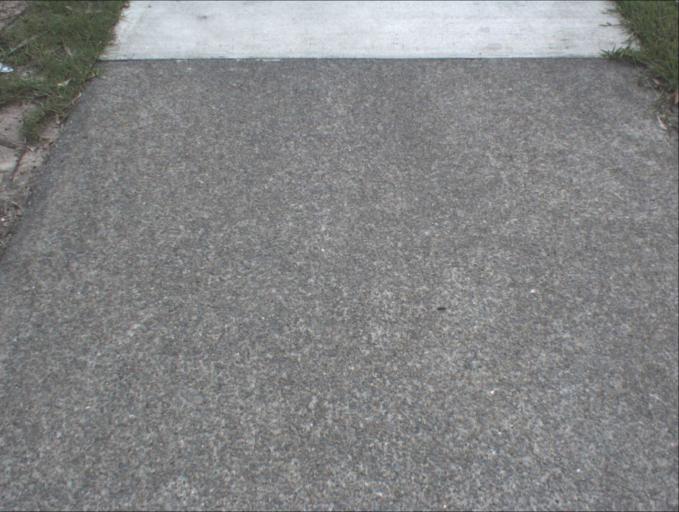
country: AU
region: Queensland
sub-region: Logan
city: Woodridge
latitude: -27.6709
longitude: 153.0583
